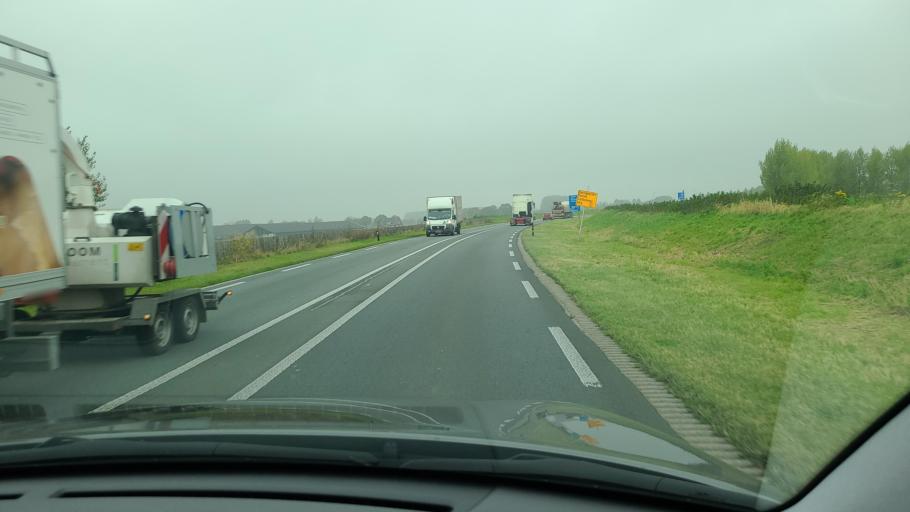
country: NL
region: Gelderland
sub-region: Gemeente Tiel
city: Tiel
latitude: 51.8714
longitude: 5.4991
